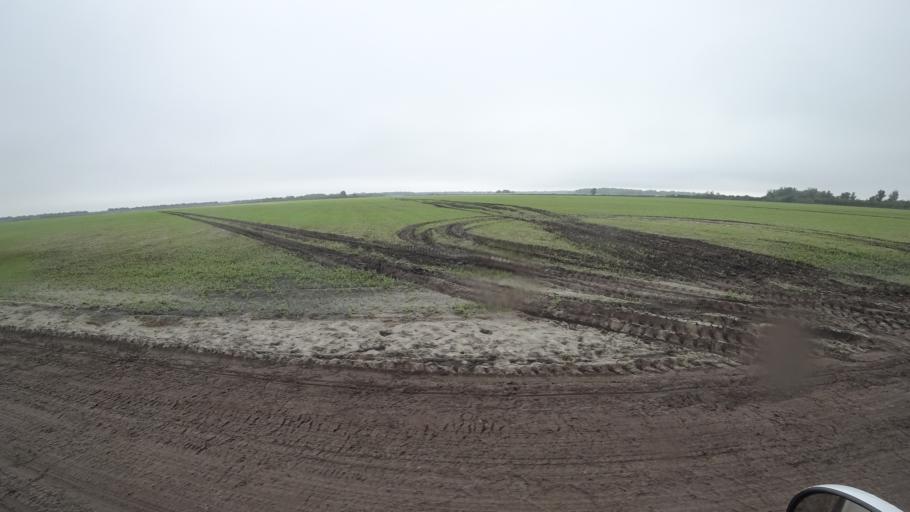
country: US
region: Florida
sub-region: Sarasota County
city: Warm Mineral Springs
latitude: 27.2987
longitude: -82.1656
